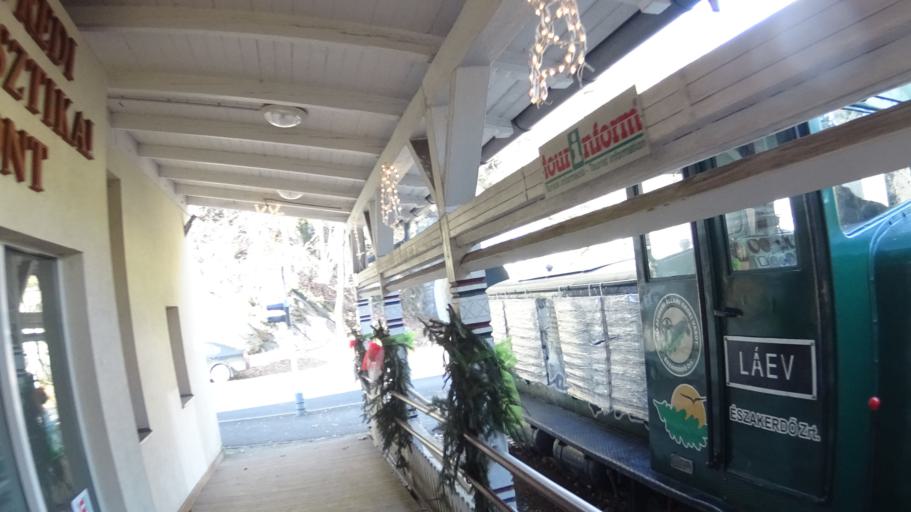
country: HU
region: Borsod-Abauj-Zemplen
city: Sajobabony
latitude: 48.1035
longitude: 20.6227
